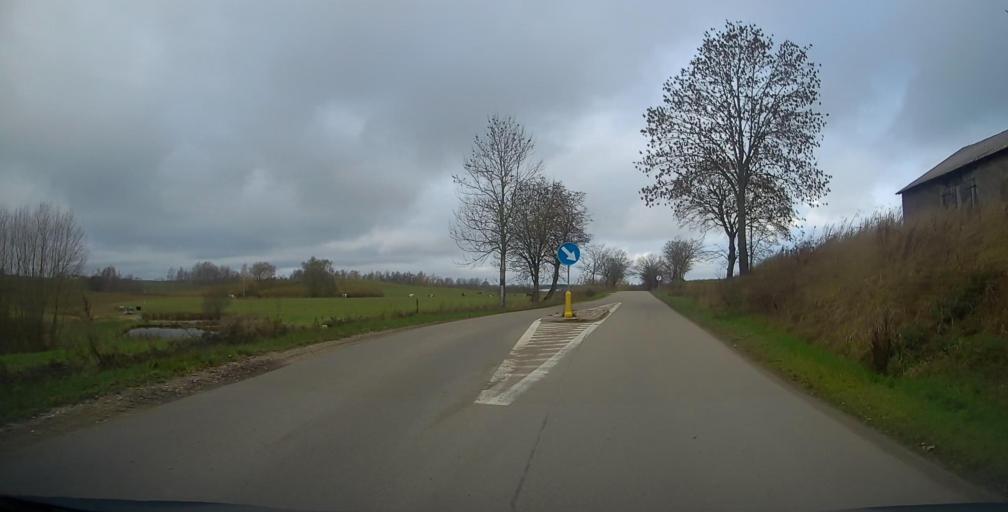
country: PL
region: Podlasie
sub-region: Suwalki
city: Suwalki
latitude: 54.3173
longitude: 22.8637
